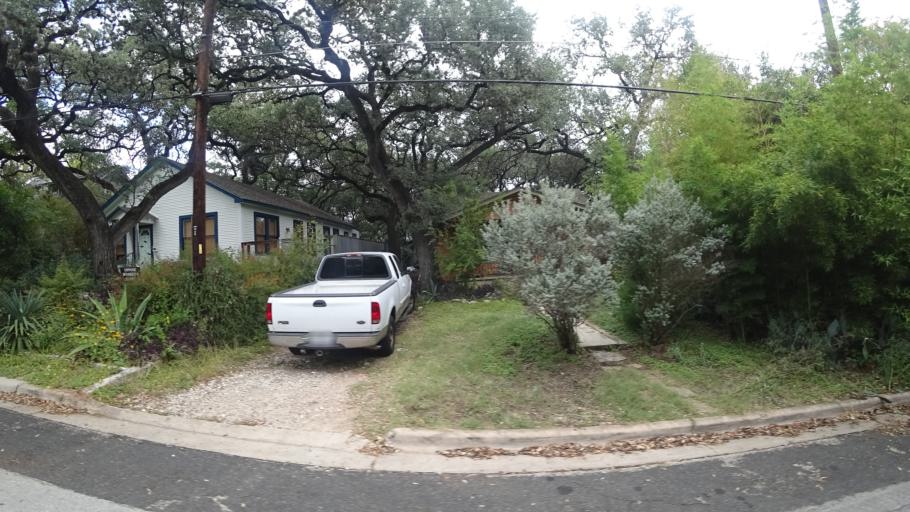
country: US
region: Texas
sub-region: Travis County
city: Austin
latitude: 30.2535
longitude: -97.7561
